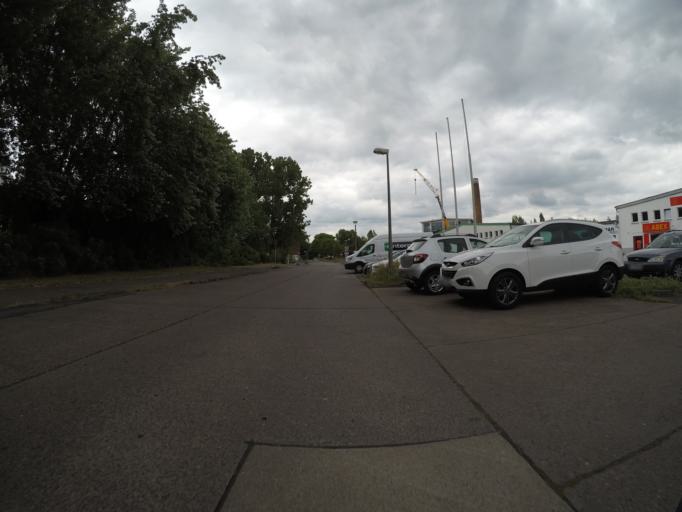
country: DE
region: Berlin
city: Rummelsburg
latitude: 52.5082
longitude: 13.4855
